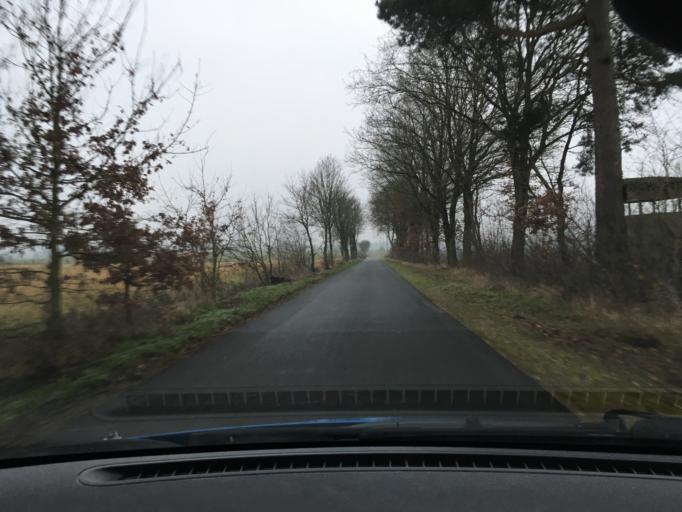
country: DE
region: Lower Saxony
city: Soderstorf
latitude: 53.0974
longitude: 10.1634
